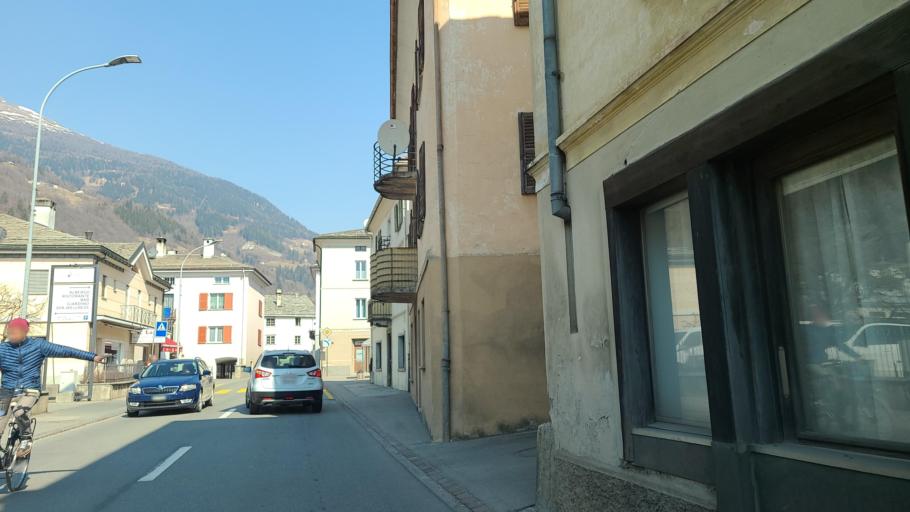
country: CH
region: Grisons
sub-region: Bernina District
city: Poschiavo
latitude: 46.3231
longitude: 10.0578
